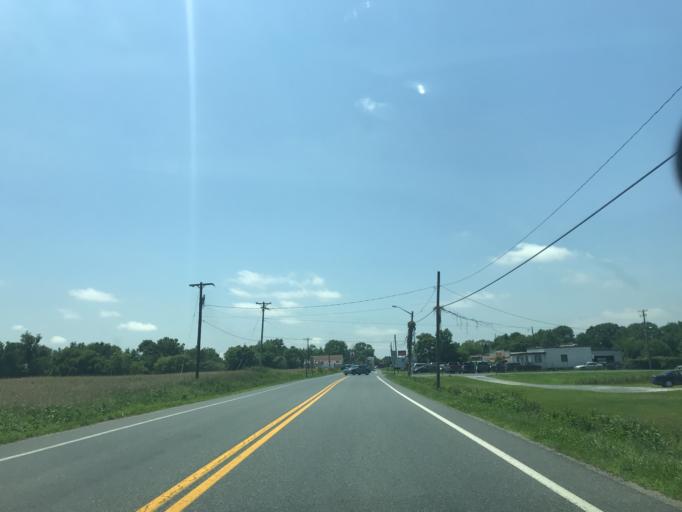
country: US
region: Maryland
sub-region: Dorchester County
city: Hurlock
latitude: 38.6301
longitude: -75.8558
